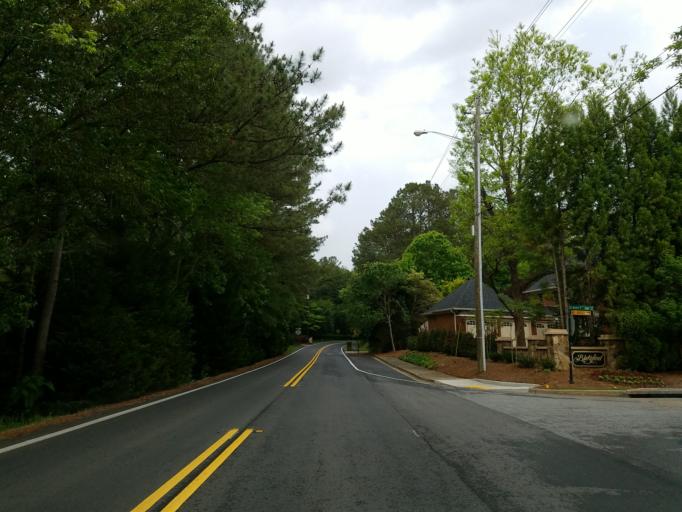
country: US
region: Georgia
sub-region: Fulton County
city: Roswell
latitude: 33.9999
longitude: -84.4458
